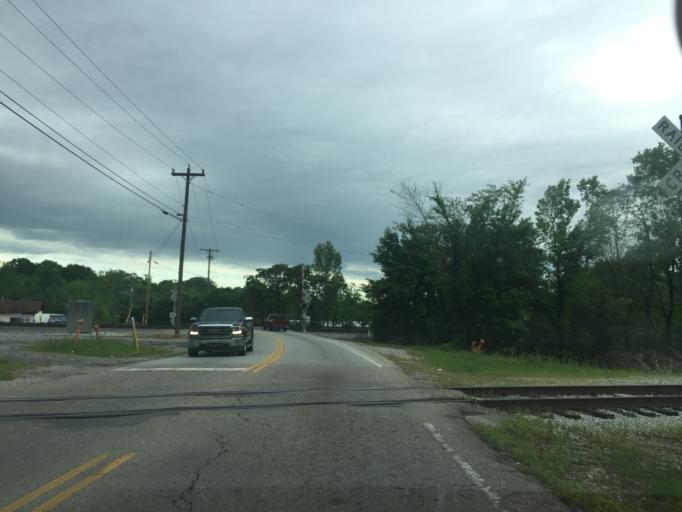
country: US
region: Tennessee
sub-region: Hamilton County
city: Harrison
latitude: 35.0674
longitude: -85.1573
